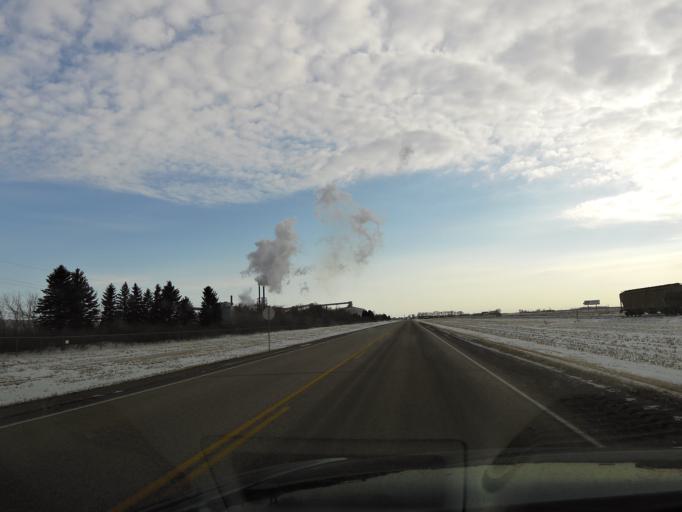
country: US
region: Minnesota
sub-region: Kittson County
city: Hallock
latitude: 48.5986
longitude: -97.1787
